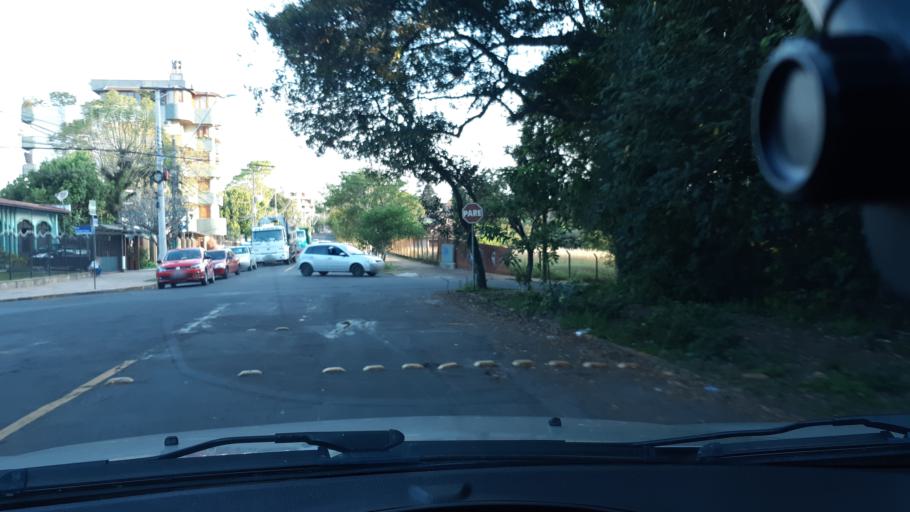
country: BR
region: Rio Grande do Sul
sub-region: Sao Leopoldo
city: Sao Leopoldo
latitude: -29.7712
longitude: -51.1363
